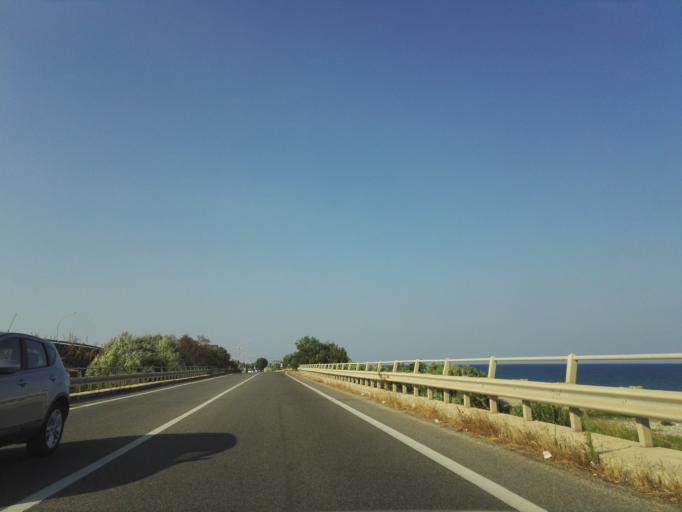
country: IT
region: Calabria
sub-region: Provincia di Reggio Calabria
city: Monasterace Marina
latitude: 38.4265
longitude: 16.5696
